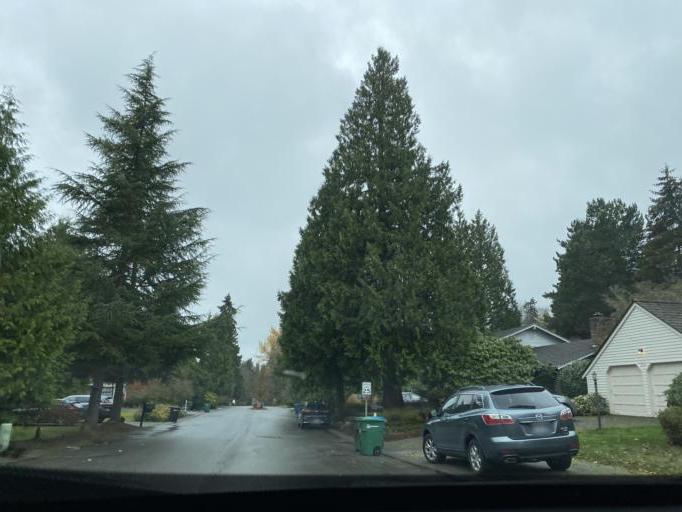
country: US
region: Washington
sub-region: King County
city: Mercer Island
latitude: 47.5480
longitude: -122.2270
